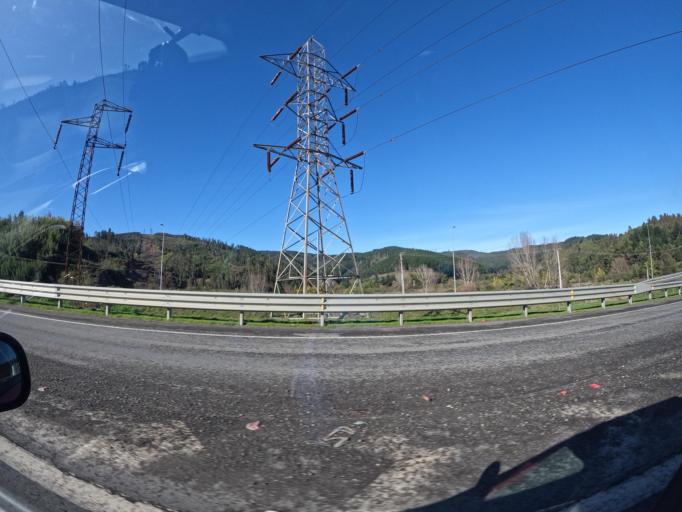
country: CL
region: Biobio
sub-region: Provincia de Concepcion
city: Concepcion
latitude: -36.8137
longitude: -72.9778
